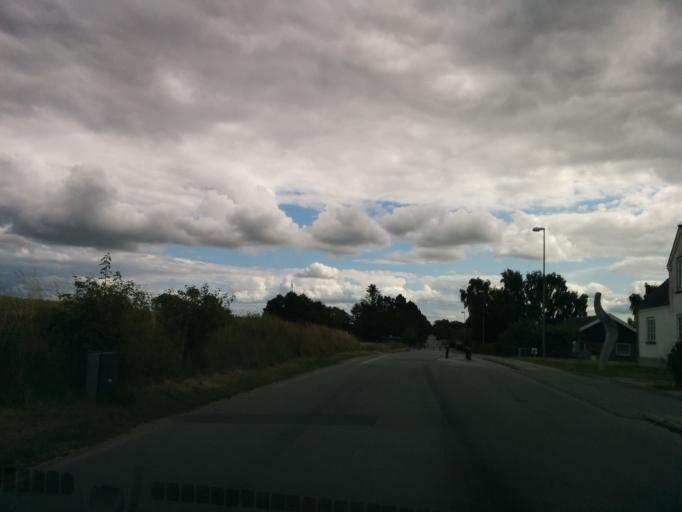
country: DK
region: Central Jutland
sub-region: Arhus Kommune
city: Kolt
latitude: 56.1254
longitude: 10.0642
